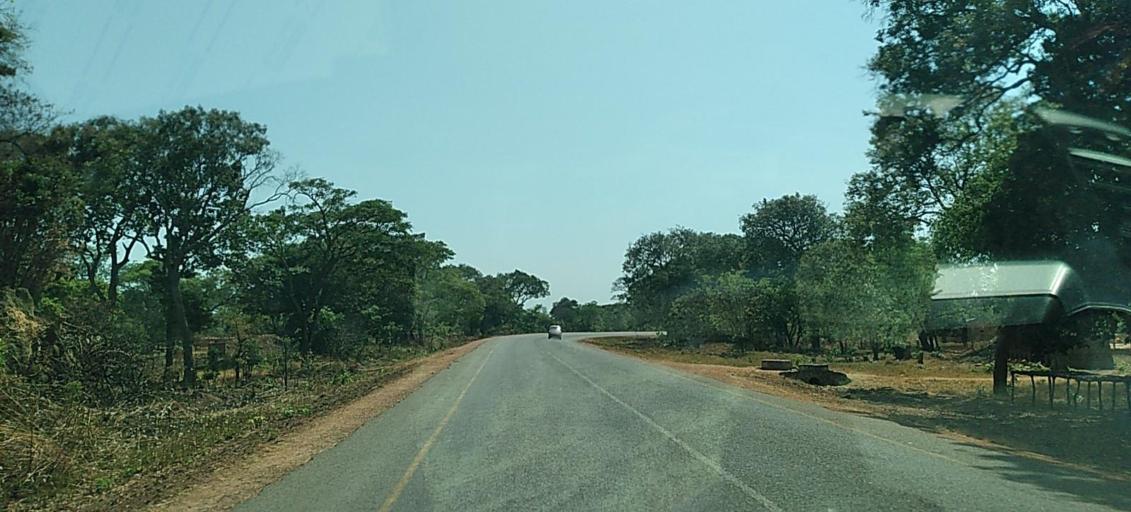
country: ZM
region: North-Western
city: Solwezi
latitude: -12.2926
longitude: 25.7175
